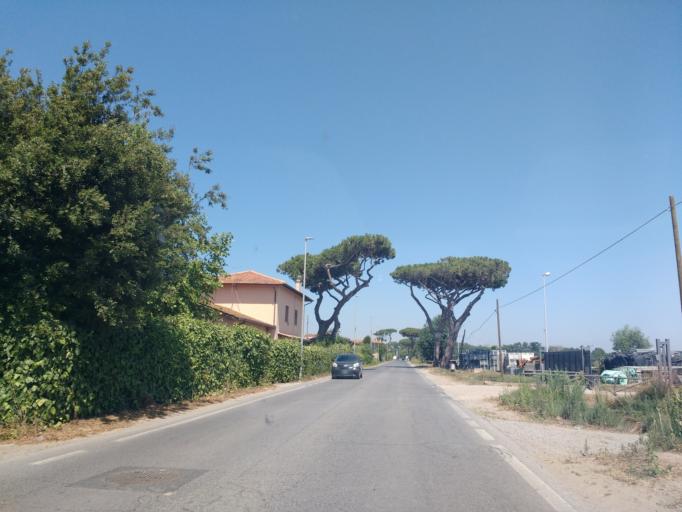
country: IT
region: Latium
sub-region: Citta metropolitana di Roma Capitale
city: Maccarese
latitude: 41.8584
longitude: 12.2147
